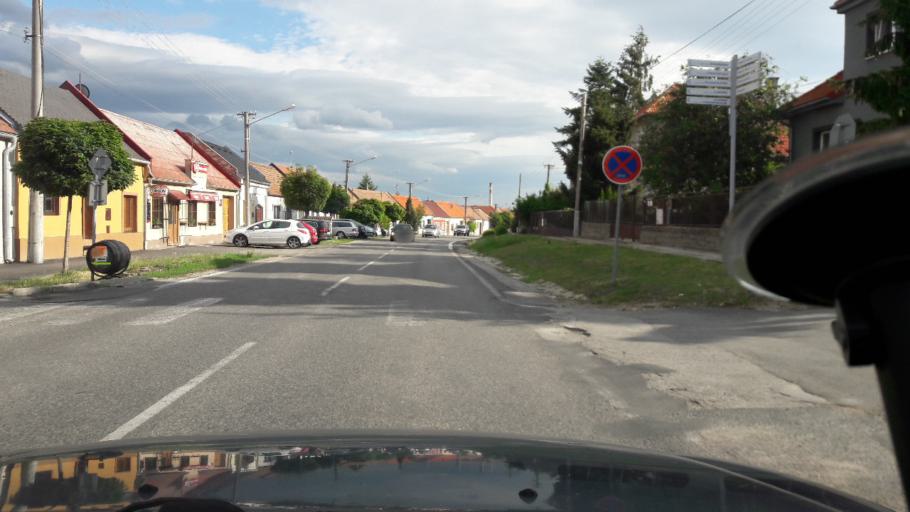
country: SK
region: Bratislavsky
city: Modra
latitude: 48.3296
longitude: 17.3048
